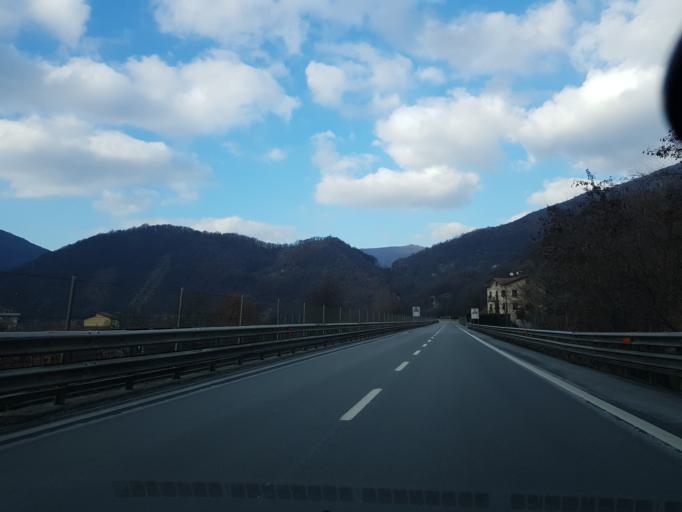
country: IT
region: Liguria
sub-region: Provincia di Genova
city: Isola del Cantone
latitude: 44.6467
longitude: 8.9595
